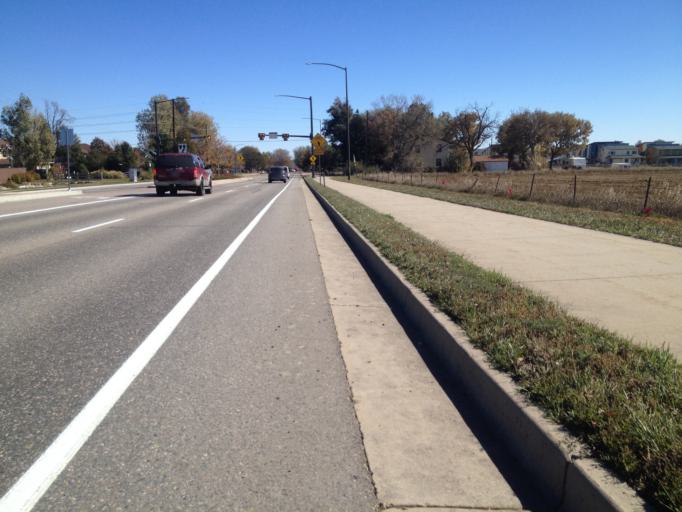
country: US
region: Colorado
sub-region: Boulder County
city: Louisville
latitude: 39.9868
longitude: -105.1200
